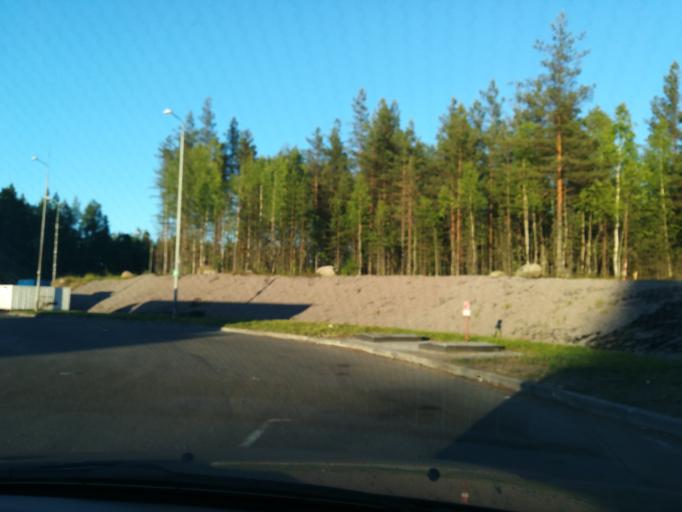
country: RU
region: Leningrad
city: Veshchevo
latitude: 60.6015
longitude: 29.1014
